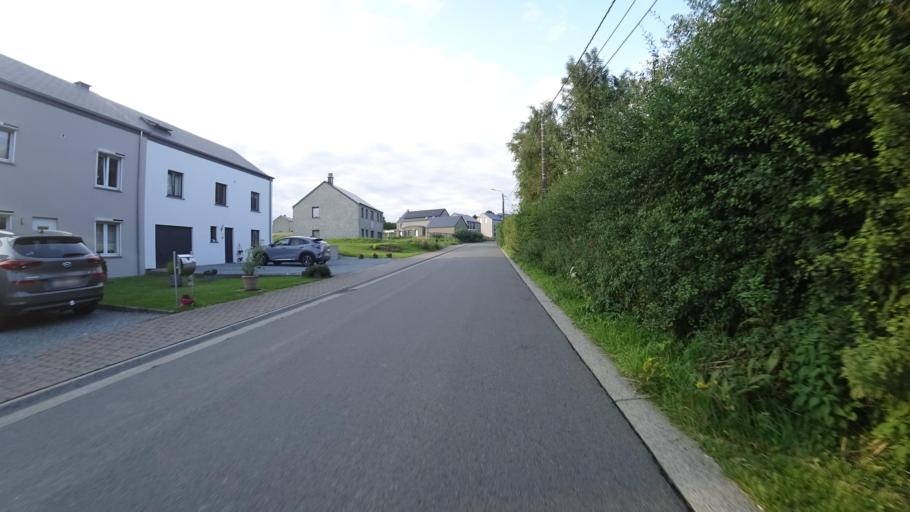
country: BE
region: Wallonia
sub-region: Province du Luxembourg
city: Neufchateau
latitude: 49.9016
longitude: 5.3861
